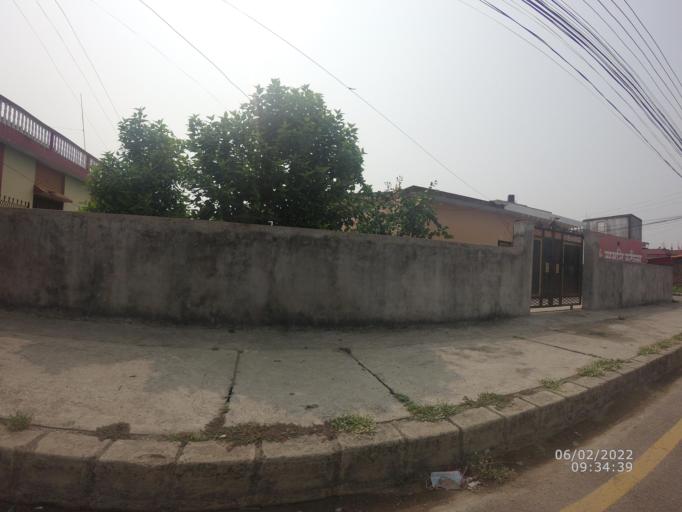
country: NP
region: Western Region
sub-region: Lumbini Zone
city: Bhairahawa
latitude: 27.4995
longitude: 83.4538
